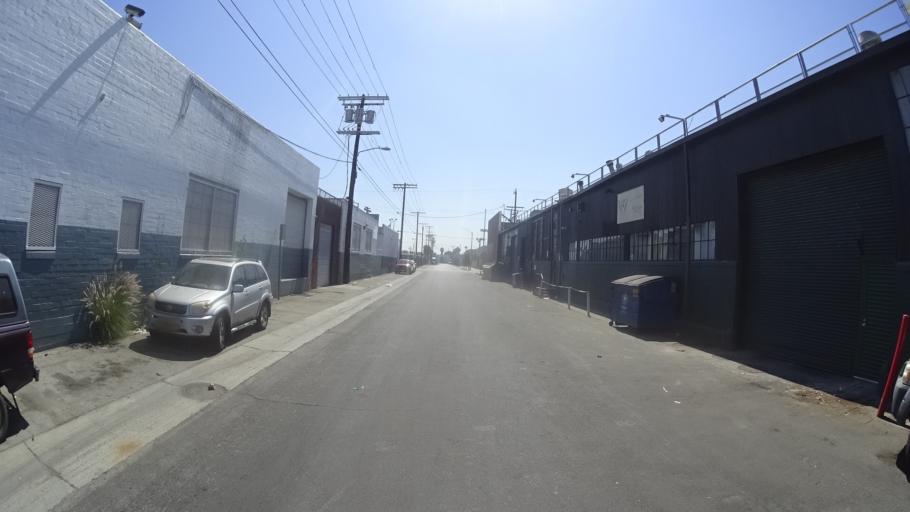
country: US
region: California
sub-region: Los Angeles County
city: View Park-Windsor Hills
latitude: 33.9852
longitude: -118.3124
